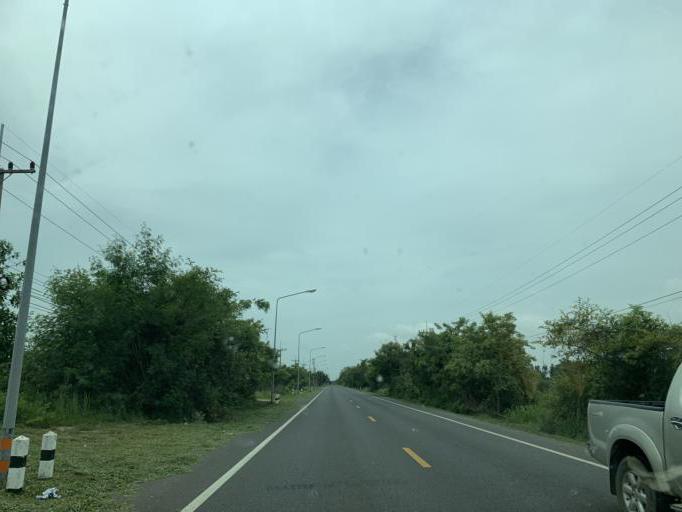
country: TH
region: Uthai Thani
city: Sawang Arom
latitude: 15.6194
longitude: 99.8415
